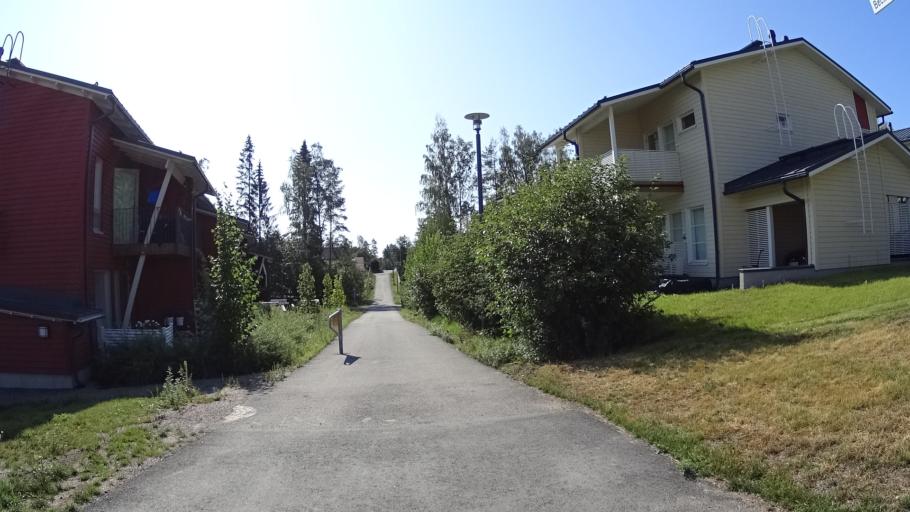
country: FI
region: Uusimaa
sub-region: Helsinki
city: Espoo
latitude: 60.1806
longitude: 24.6038
